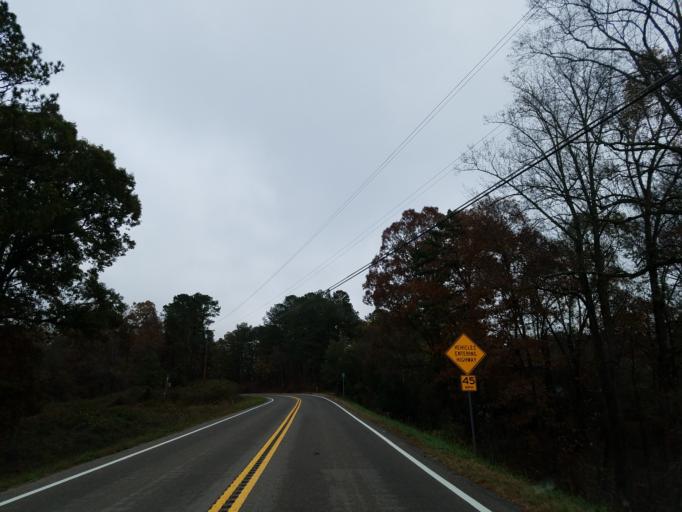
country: US
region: Georgia
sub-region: Cherokee County
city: Canton
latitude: 34.2644
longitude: -84.5879
